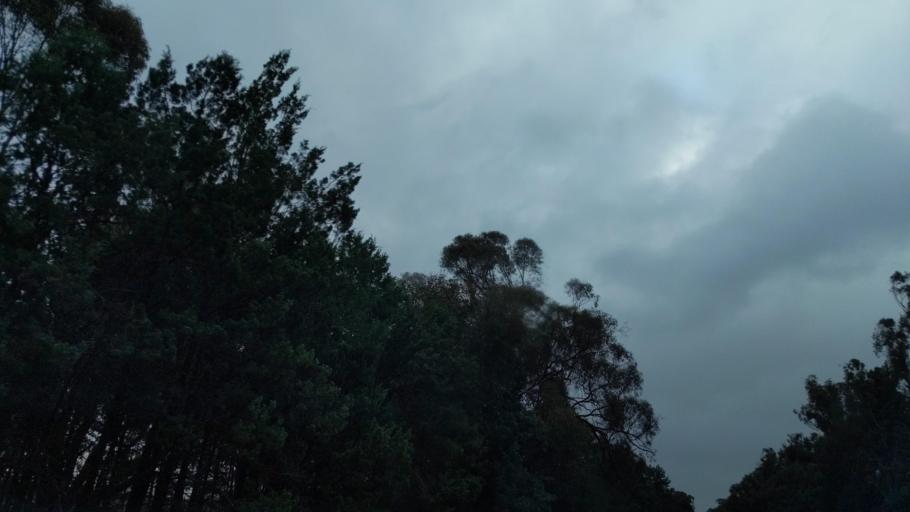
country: AU
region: New South Wales
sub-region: Coolamon
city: Coolamon
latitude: -34.9360
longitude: 147.3002
